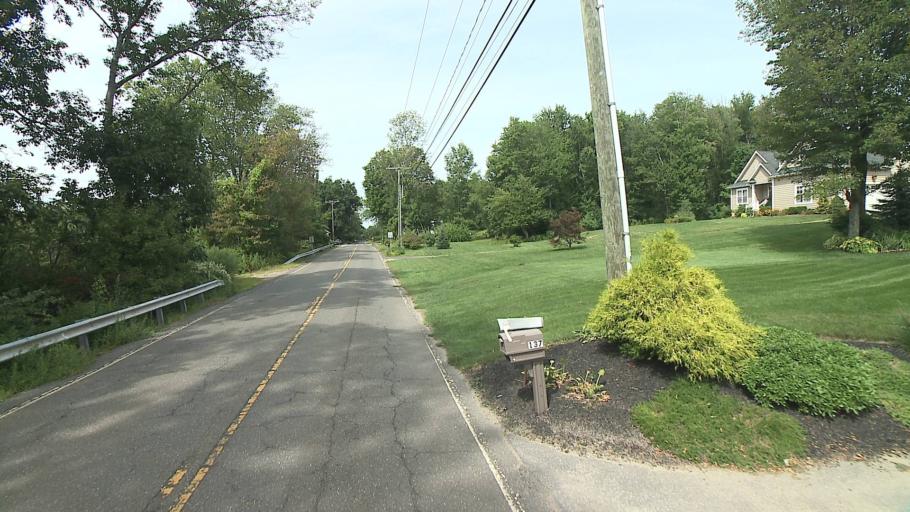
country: US
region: Connecticut
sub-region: Litchfield County
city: Plymouth
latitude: 41.6359
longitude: -73.0507
